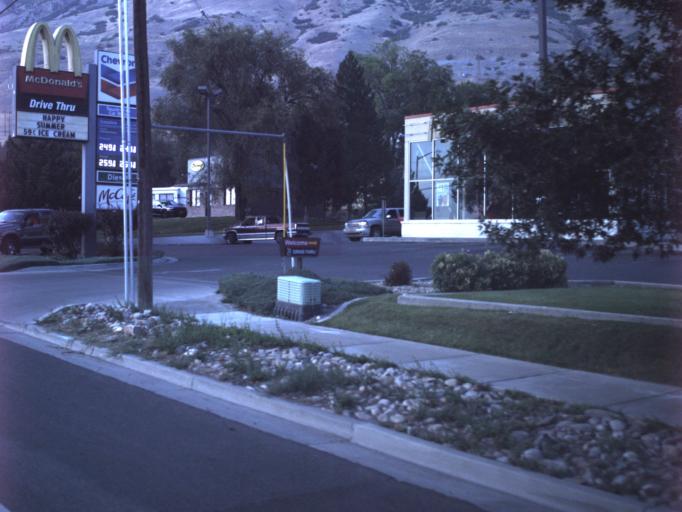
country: US
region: Utah
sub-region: Utah County
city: Springville
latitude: 40.1860
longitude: -111.6106
